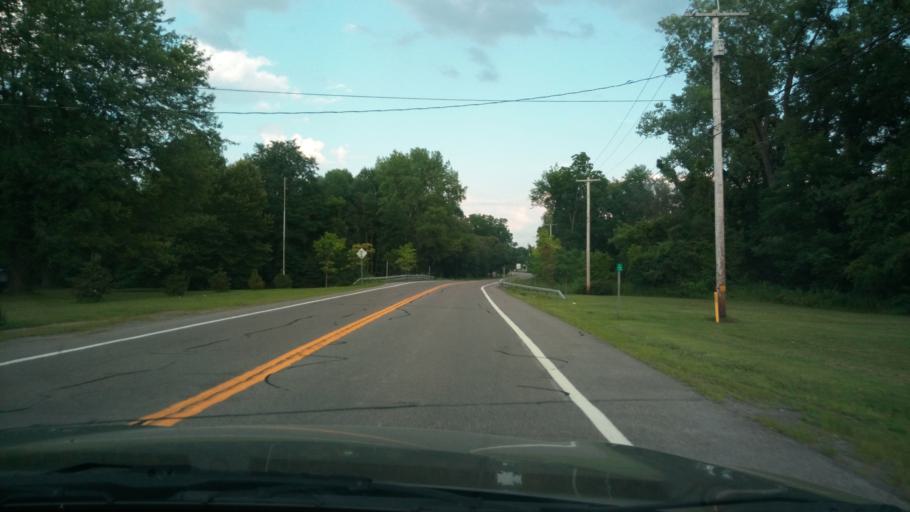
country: US
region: New York
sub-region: Wayne County
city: Clyde
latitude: 43.0895
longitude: -76.8923
